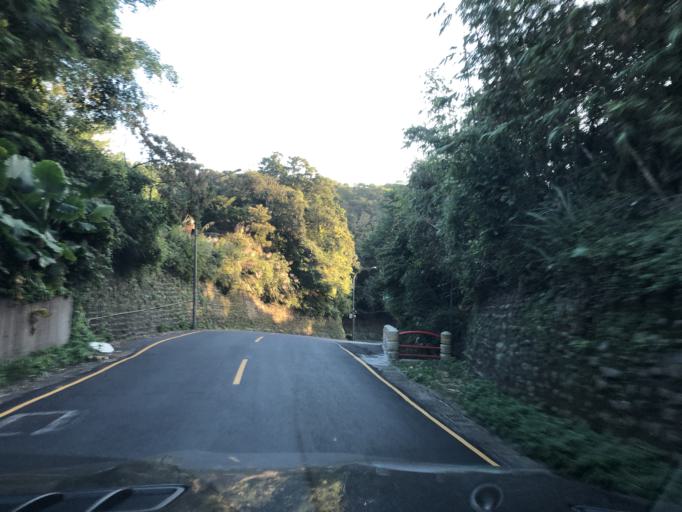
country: TW
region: Taipei
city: Taipei
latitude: 25.1431
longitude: 121.5567
